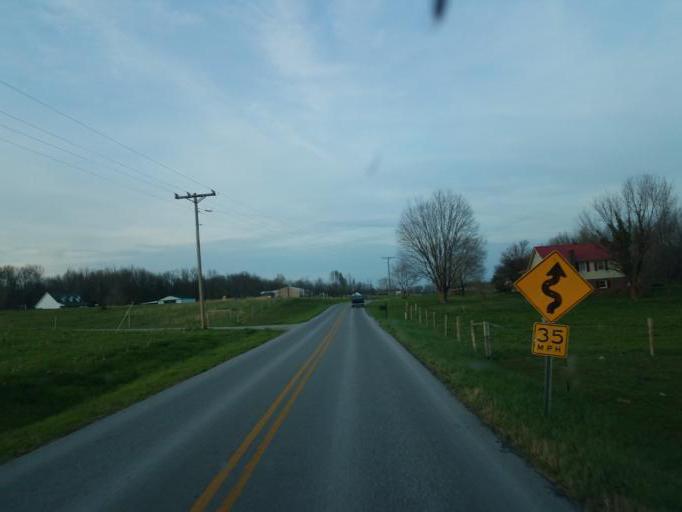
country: US
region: Kentucky
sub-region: Metcalfe County
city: Edmonton
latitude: 37.1504
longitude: -85.6897
